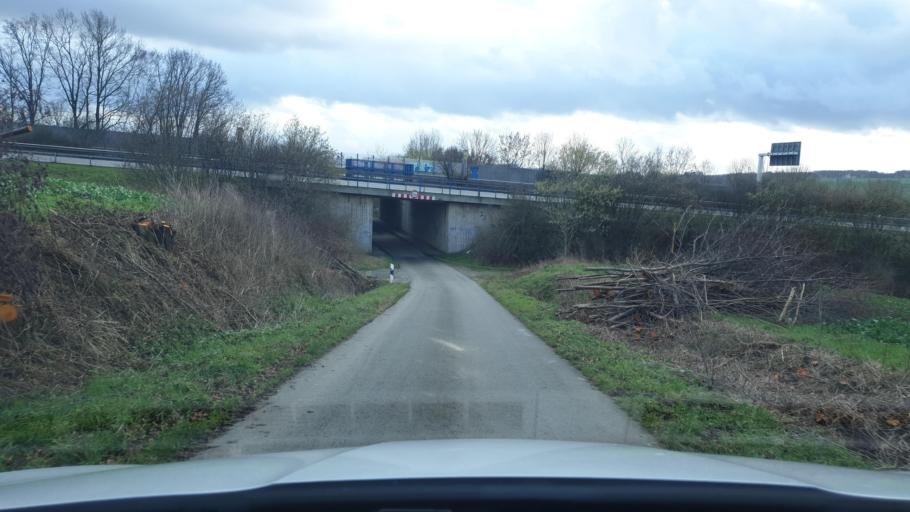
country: DE
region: North Rhine-Westphalia
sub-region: Regierungsbezirk Detmold
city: Bad Salzuflen
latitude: 52.1417
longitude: 8.7746
